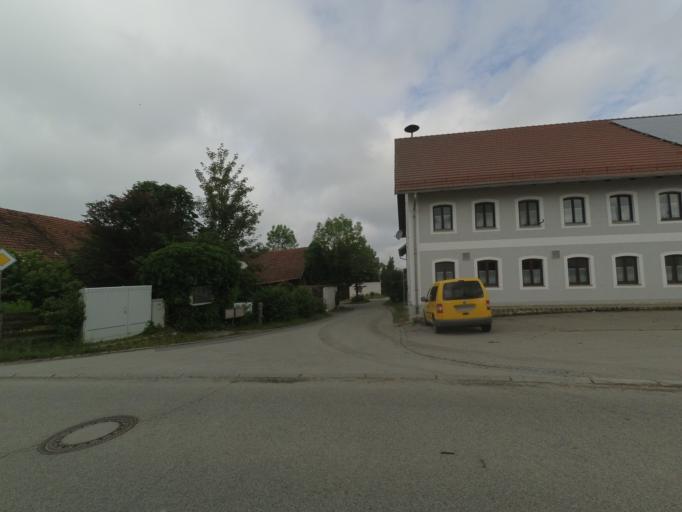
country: DE
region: Bavaria
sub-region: Lower Bavaria
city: Perkam
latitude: 48.8459
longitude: 12.4229
